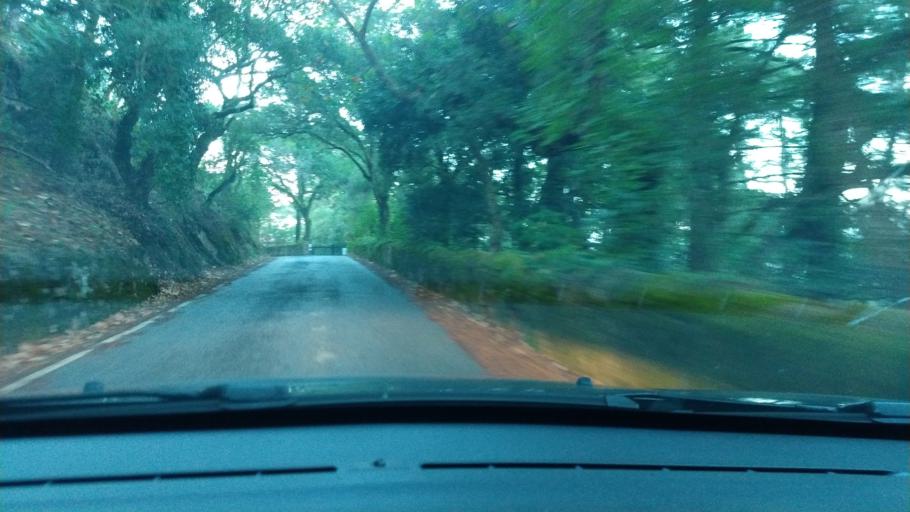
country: PT
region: Lisbon
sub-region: Sintra
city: Colares
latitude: 38.7913
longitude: -9.4168
